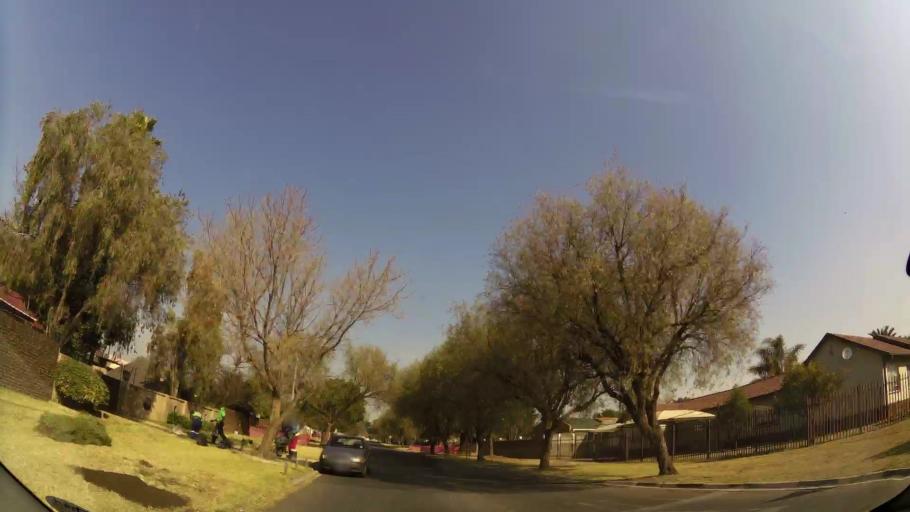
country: ZA
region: Gauteng
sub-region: Ekurhuleni Metropolitan Municipality
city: Benoni
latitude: -26.1501
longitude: 28.2838
